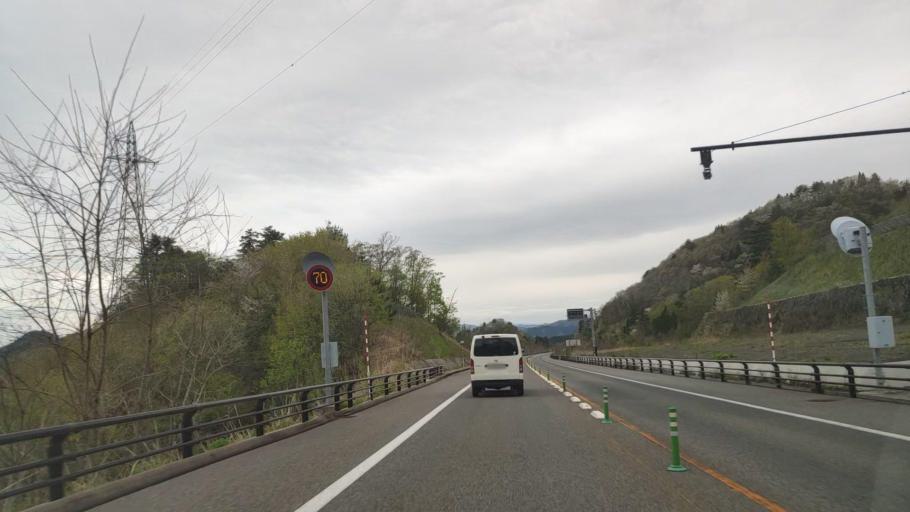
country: JP
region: Akita
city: Odate
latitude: 40.3229
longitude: 140.5982
